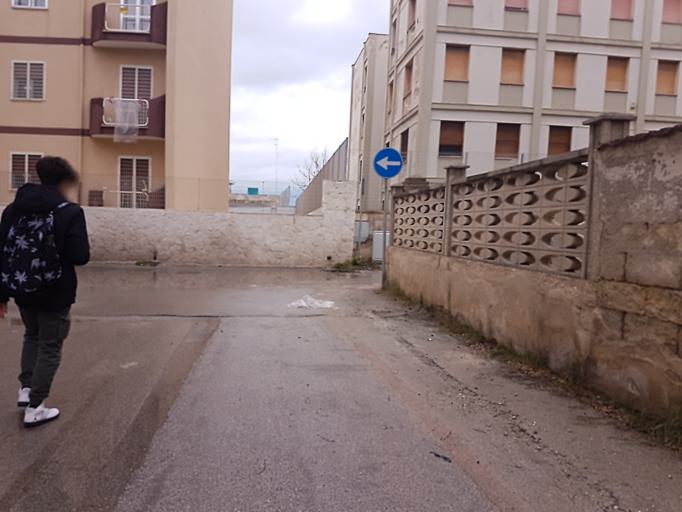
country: IT
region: Apulia
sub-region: Provincia di Bari
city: San Paolo
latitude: 41.1388
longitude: 16.8117
